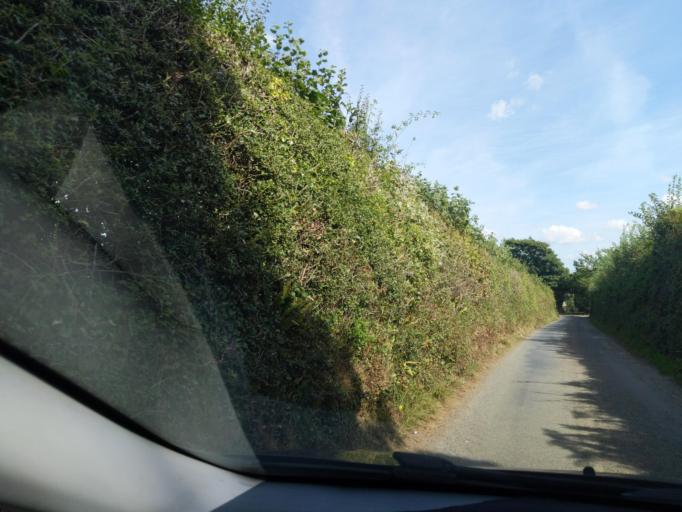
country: GB
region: England
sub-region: Cornwall
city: Torpoint
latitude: 50.3588
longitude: -4.2305
